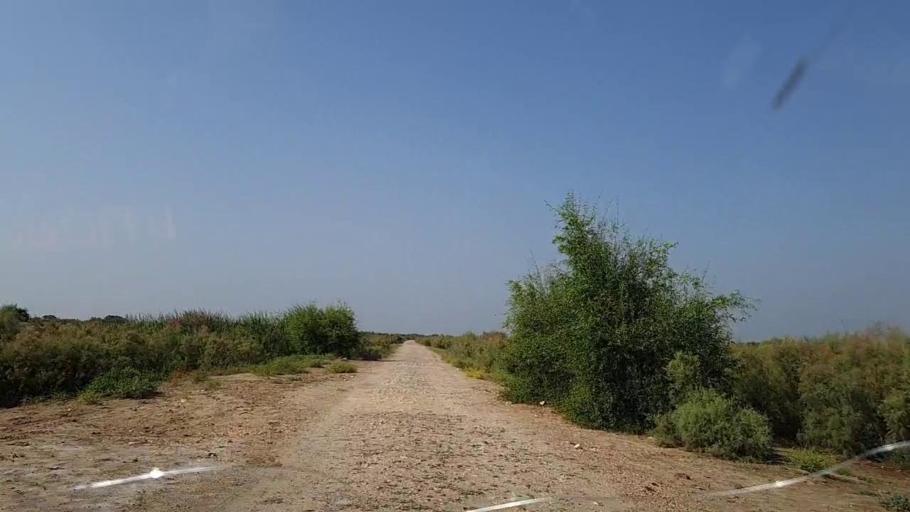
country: PK
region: Sindh
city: Khanpur
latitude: 27.7001
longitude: 69.3854
